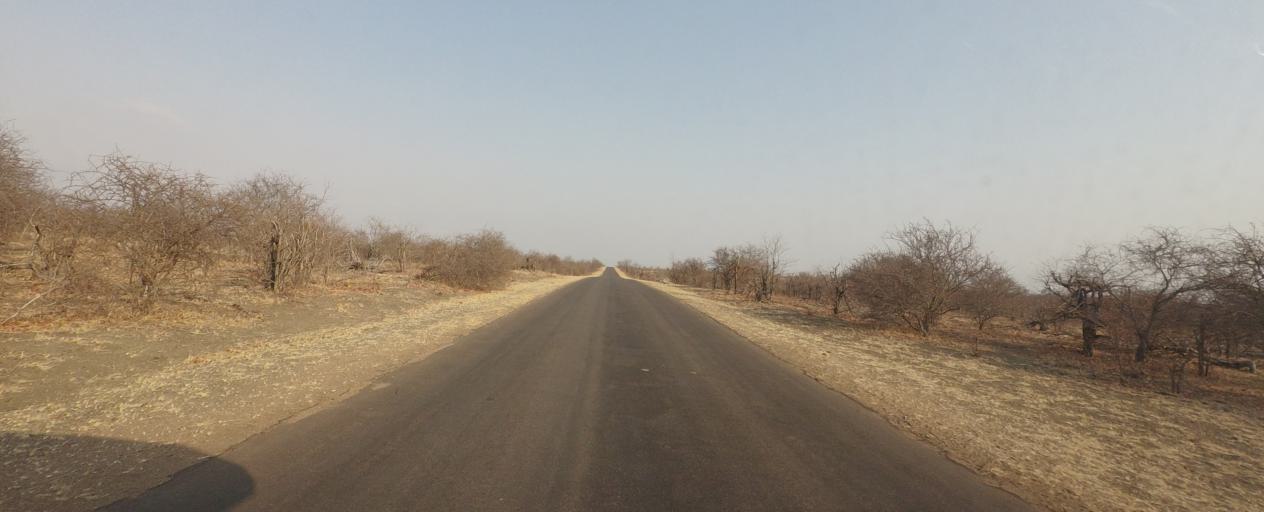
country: ZA
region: Limpopo
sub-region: Mopani District Municipality
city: Giyani
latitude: -23.0826
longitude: 31.4182
